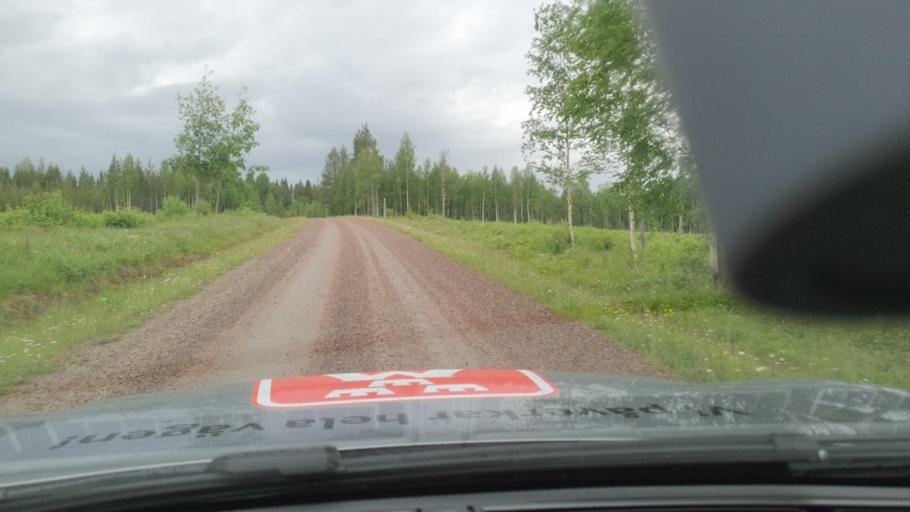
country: SE
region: Norrbotten
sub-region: Overkalix Kommun
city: OEverkalix
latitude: 66.6056
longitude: 22.7469
